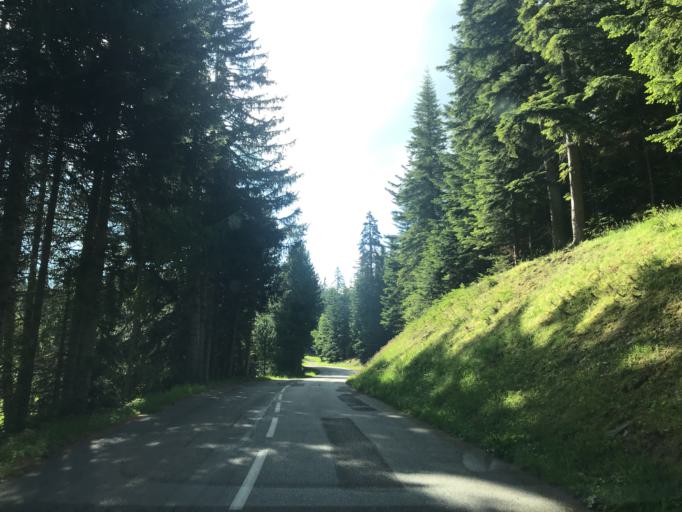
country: FR
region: Rhone-Alpes
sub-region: Departement de la Savoie
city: Modane
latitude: 45.2102
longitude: 6.6442
